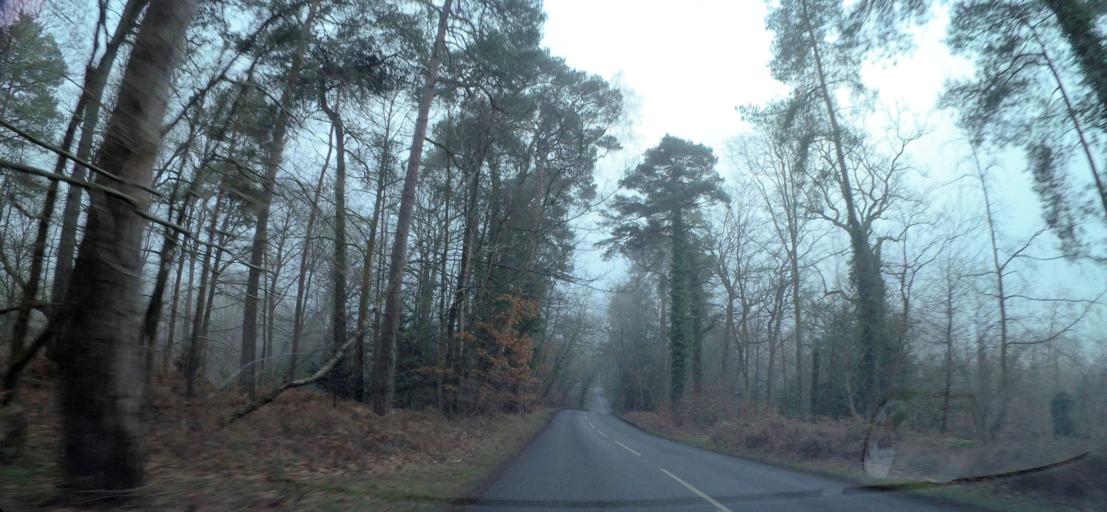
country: GB
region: England
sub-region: West Berkshire
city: Stratfield Mortimer
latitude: 51.3872
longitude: -1.0711
